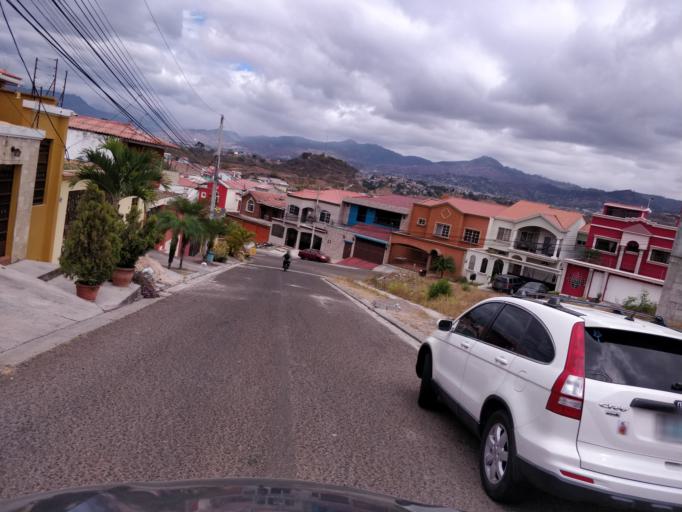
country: HN
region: Francisco Morazan
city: Yaguacire
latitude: 14.0475
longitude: -87.2170
